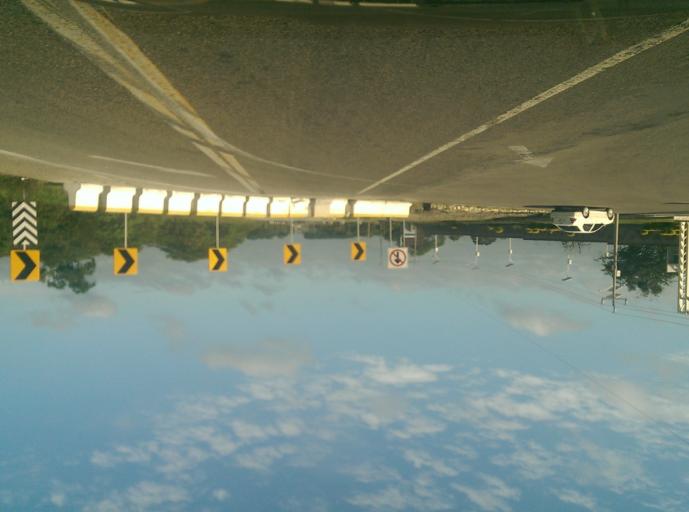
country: MX
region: Chiapas
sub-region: Catazaja
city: Catazaja
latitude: 17.7095
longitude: -92.0190
